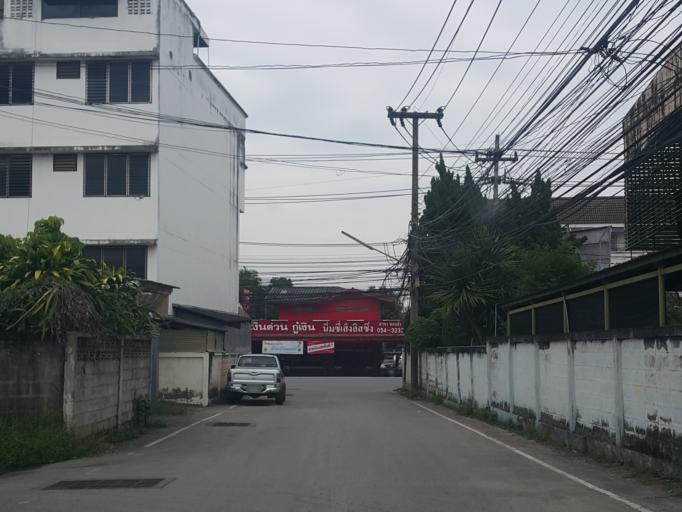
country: TH
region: Lampang
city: Lampang
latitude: 18.2907
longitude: 99.5127
